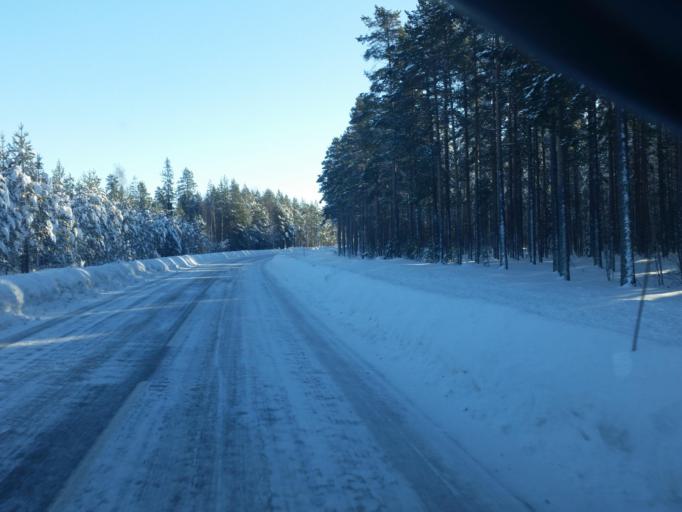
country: SE
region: Norrbotten
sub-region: Pitea Kommun
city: Roknas
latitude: 65.3529
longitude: 21.0930
